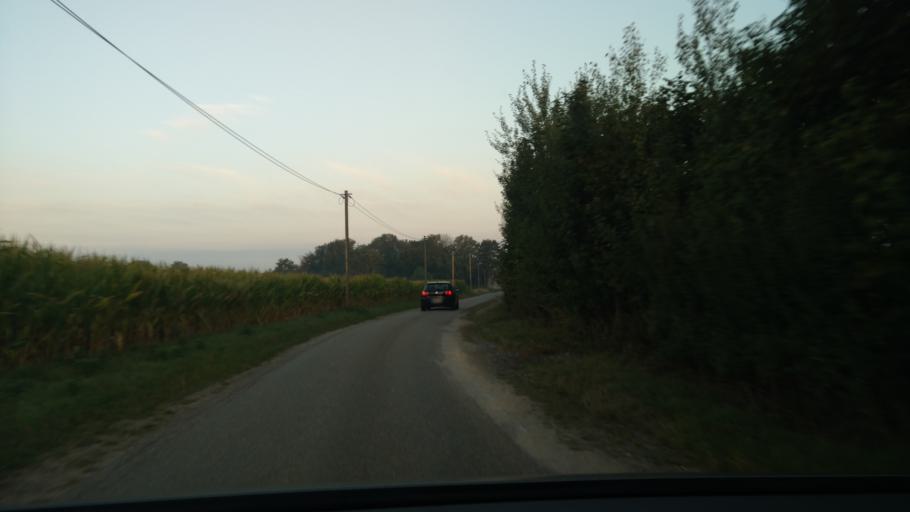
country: DE
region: North Rhine-Westphalia
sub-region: Regierungsbezirk Munster
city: Velen
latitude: 51.8583
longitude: 6.9838
